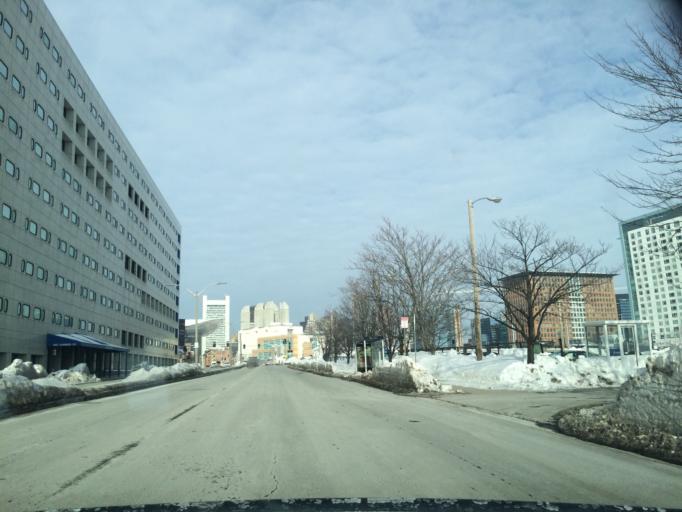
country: US
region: Massachusetts
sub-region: Suffolk County
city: South Boston
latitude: 42.3453
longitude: -71.0406
